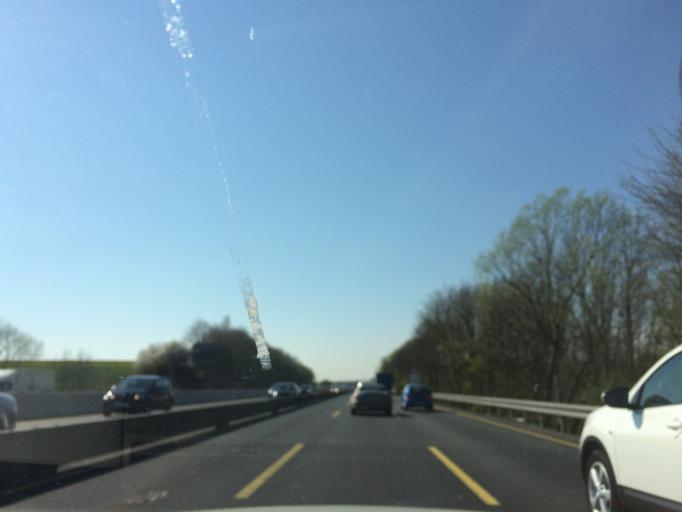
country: DE
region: North Rhine-Westphalia
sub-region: Regierungsbezirk Dusseldorf
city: Erkrath
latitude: 51.2462
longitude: 6.9115
